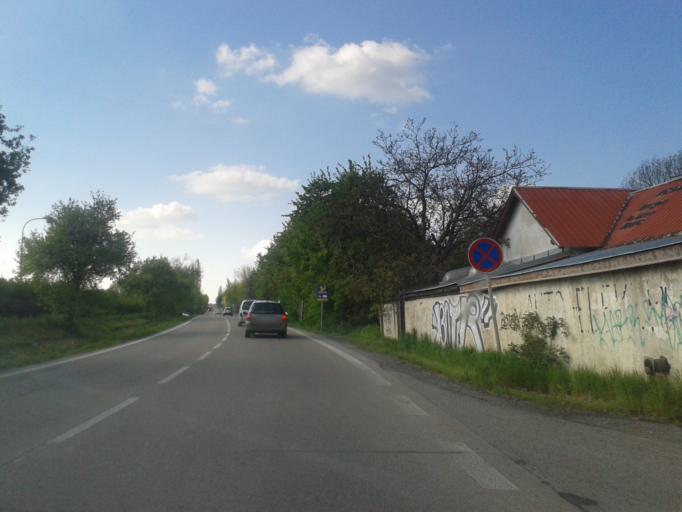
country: CZ
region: Central Bohemia
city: Hostivice
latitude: 50.0842
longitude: 14.3097
